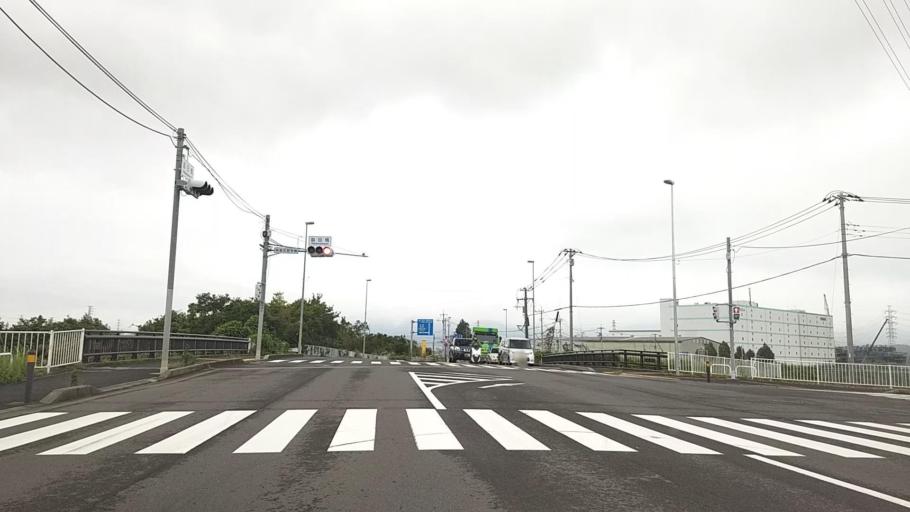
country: JP
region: Kanagawa
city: Isehara
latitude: 35.4017
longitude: 139.3398
